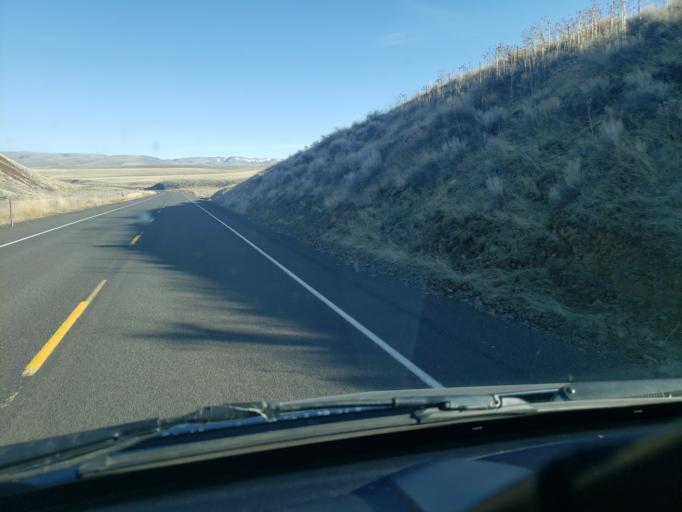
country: US
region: Oregon
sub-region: Umatilla County
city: Pilot Rock
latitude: 45.4649
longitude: -118.9070
